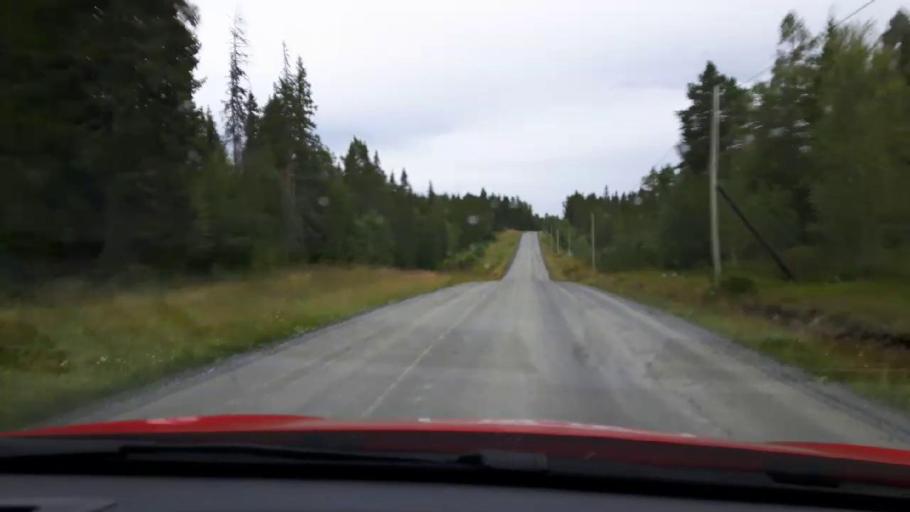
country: SE
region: Jaemtland
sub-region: Are Kommun
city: Jarpen
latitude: 63.4218
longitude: 13.3468
